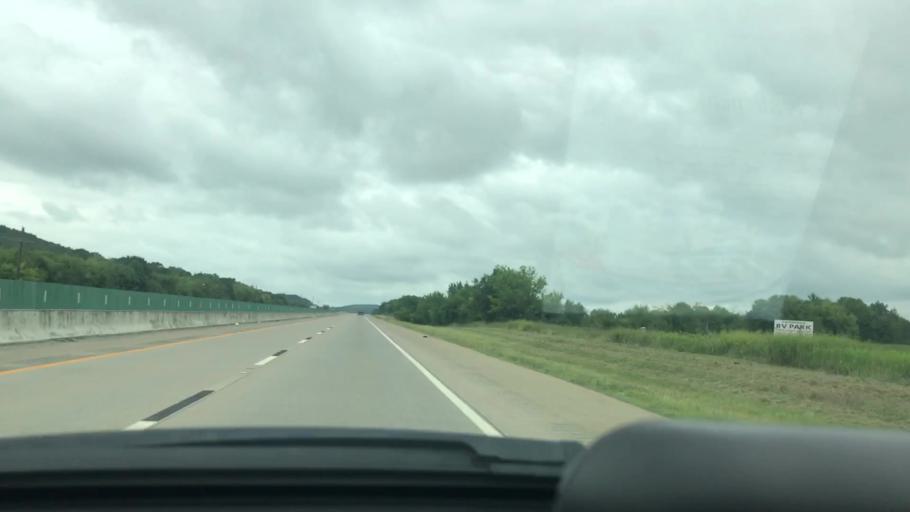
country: US
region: Oklahoma
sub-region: Pittsburg County
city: Krebs
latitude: 35.0700
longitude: -95.7049
